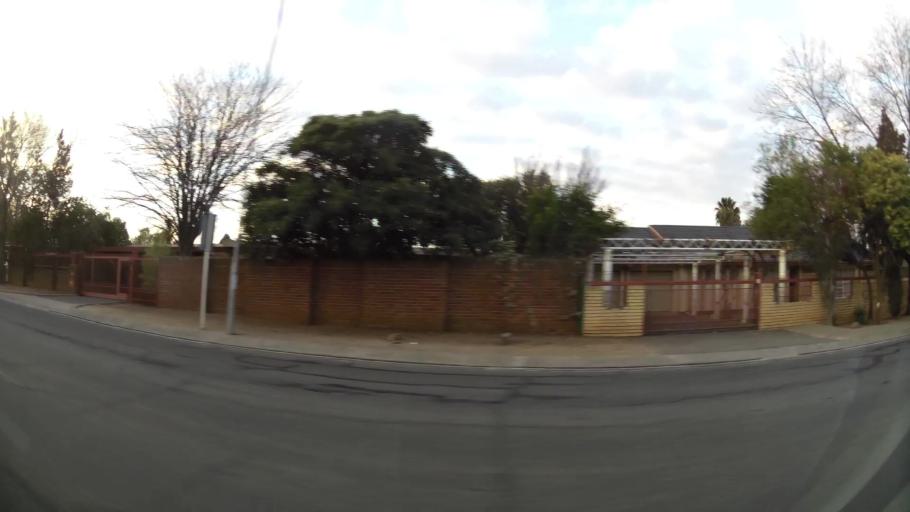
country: ZA
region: Orange Free State
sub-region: Mangaung Metropolitan Municipality
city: Bloemfontein
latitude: -29.1553
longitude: 26.1860
